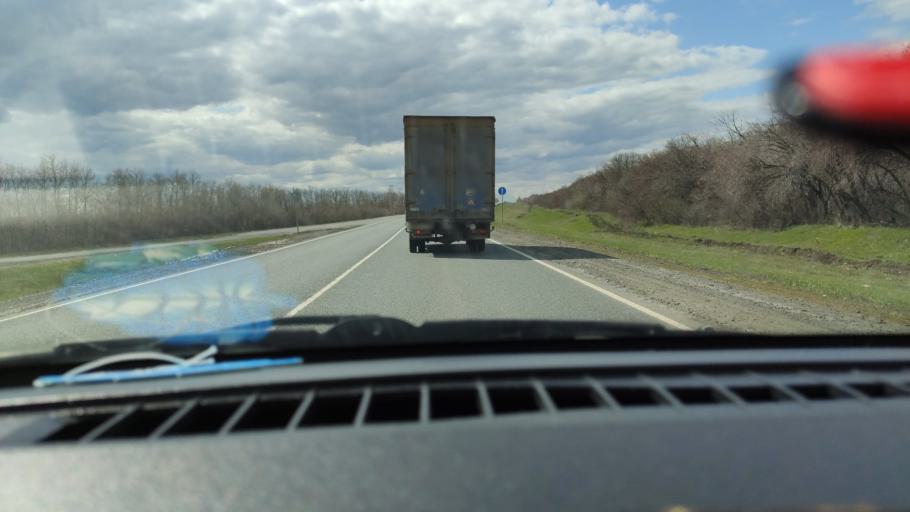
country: RU
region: Saratov
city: Balakovo
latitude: 52.1043
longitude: 47.7405
